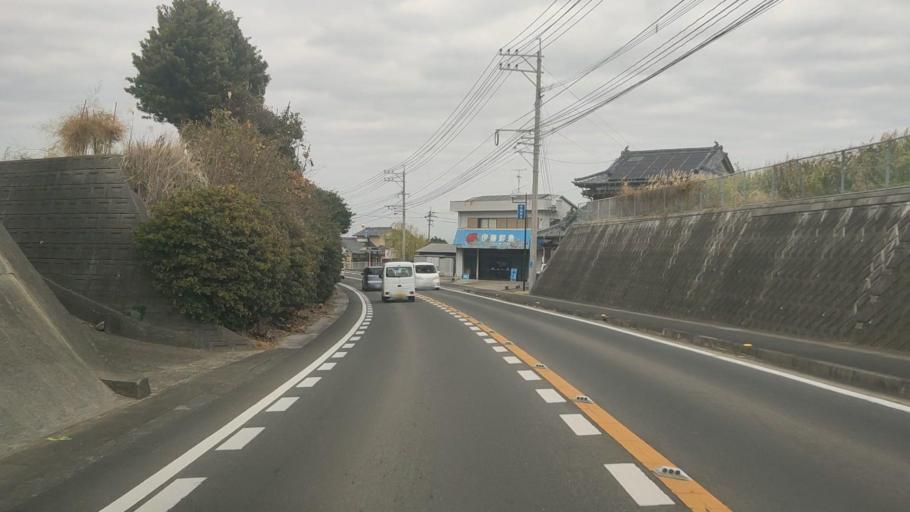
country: JP
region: Nagasaki
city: Shimabara
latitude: 32.8542
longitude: 130.3382
